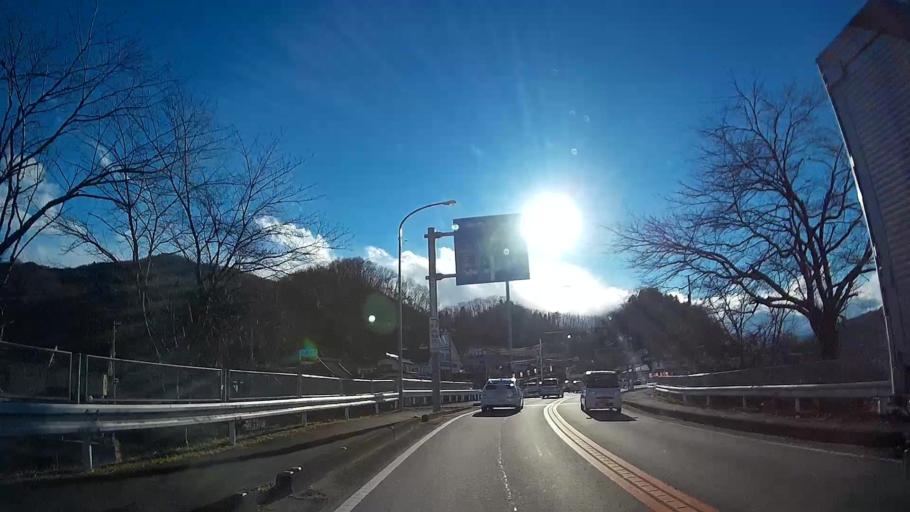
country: JP
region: Saitama
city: Yorii
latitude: 36.0784
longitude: 139.1103
